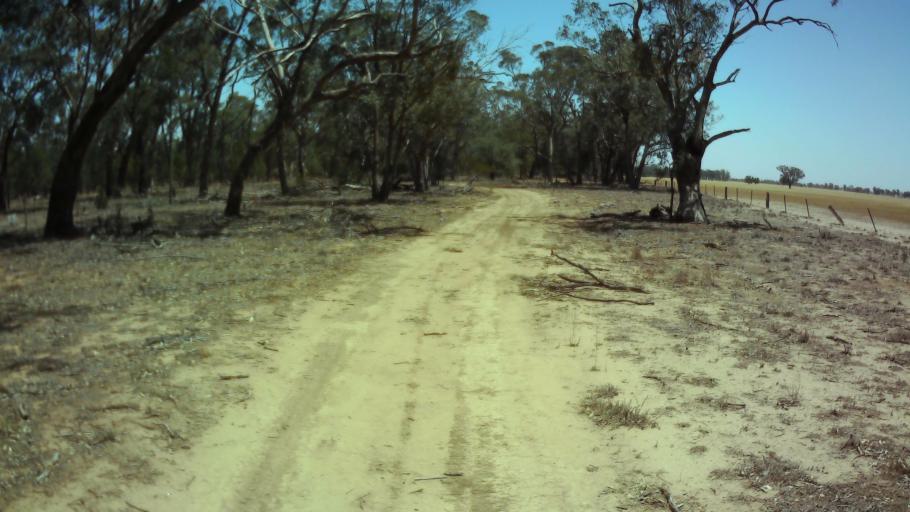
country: AU
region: New South Wales
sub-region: Weddin
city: Grenfell
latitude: -34.0634
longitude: 147.8051
